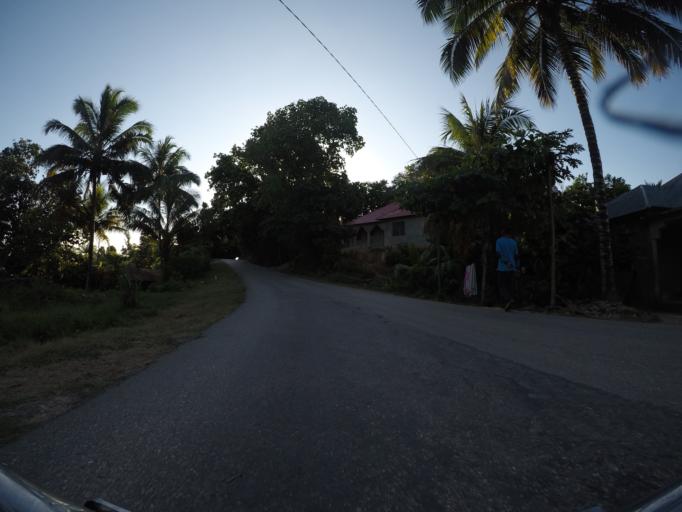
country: TZ
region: Pemba South
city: Mtambile
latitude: -5.3793
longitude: 39.6847
